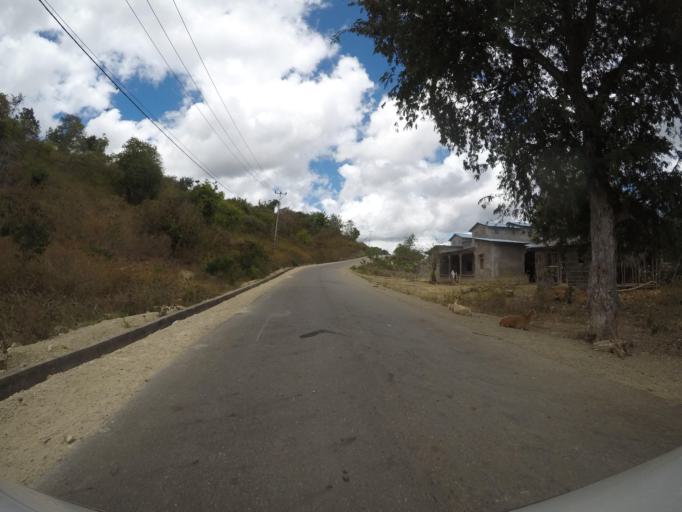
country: TL
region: Lautem
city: Lospalos
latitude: -8.3739
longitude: 126.9263
